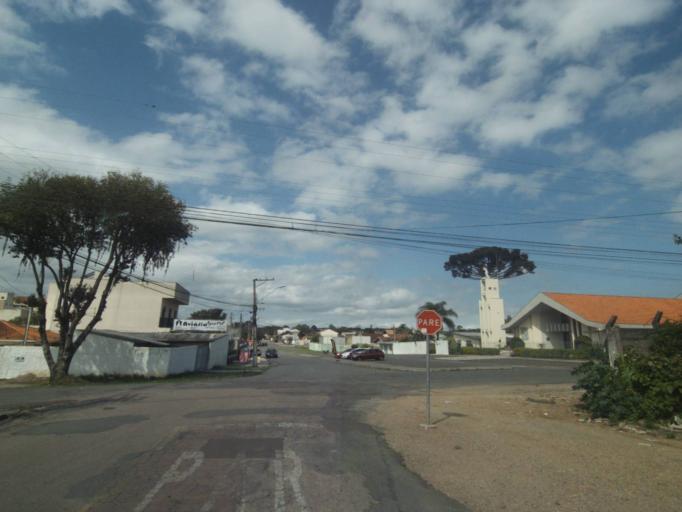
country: BR
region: Parana
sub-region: Pinhais
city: Pinhais
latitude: -25.4104
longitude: -49.2010
